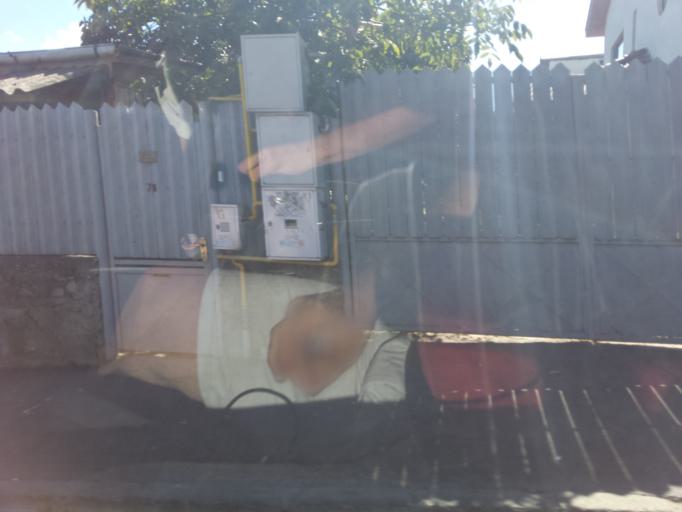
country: RO
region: Tulcea
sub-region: Municipiul Tulcea
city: Tulcea
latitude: 45.1696
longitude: 28.7922
